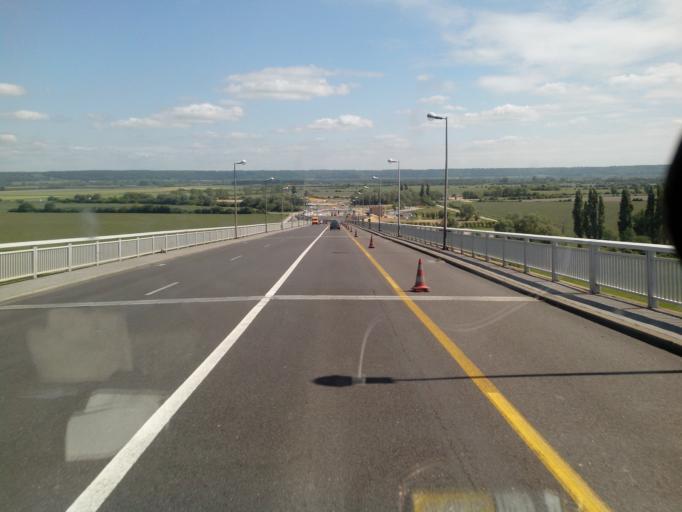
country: FR
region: Haute-Normandie
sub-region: Departement de la Seine-Maritime
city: Tancarville
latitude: 49.4682
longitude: 0.4693
